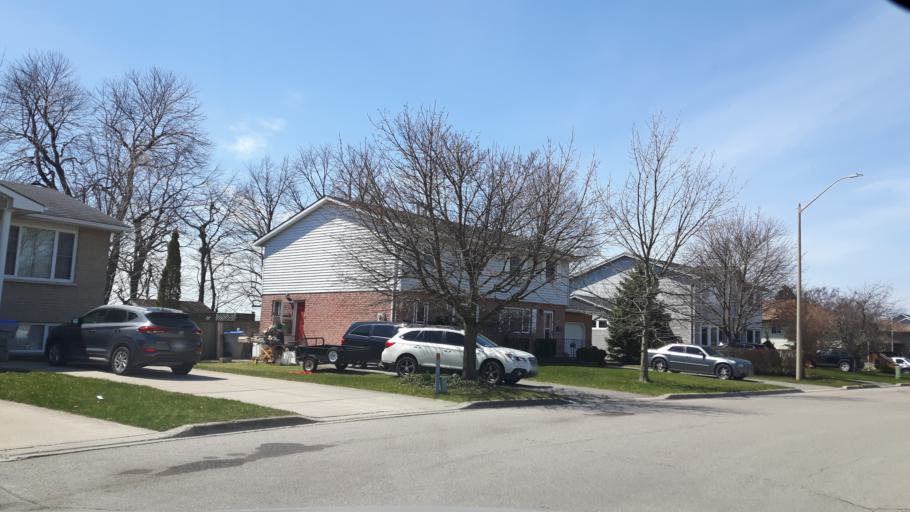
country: CA
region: Ontario
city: Goderich
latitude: 43.7285
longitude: -81.7116
